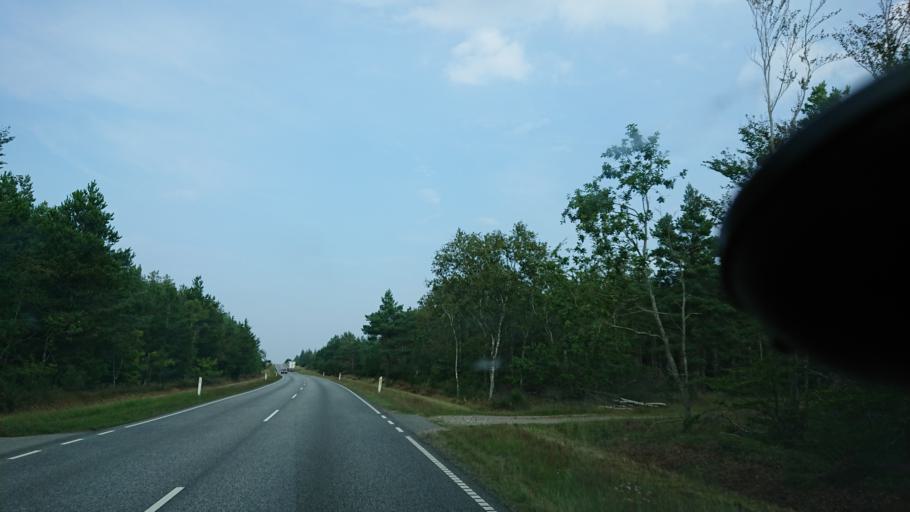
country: DK
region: North Denmark
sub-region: Frederikshavn Kommune
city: Skagen
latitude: 57.6486
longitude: 10.4609
